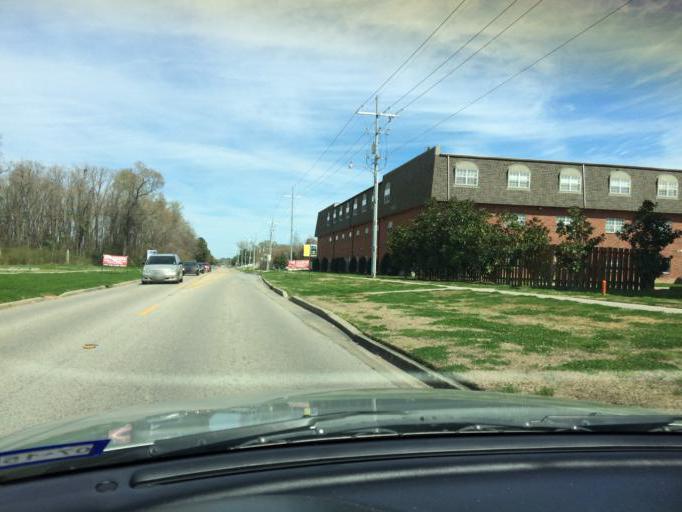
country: US
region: Louisiana
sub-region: Lafayette Parish
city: Scott
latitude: 30.2165
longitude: -92.0604
